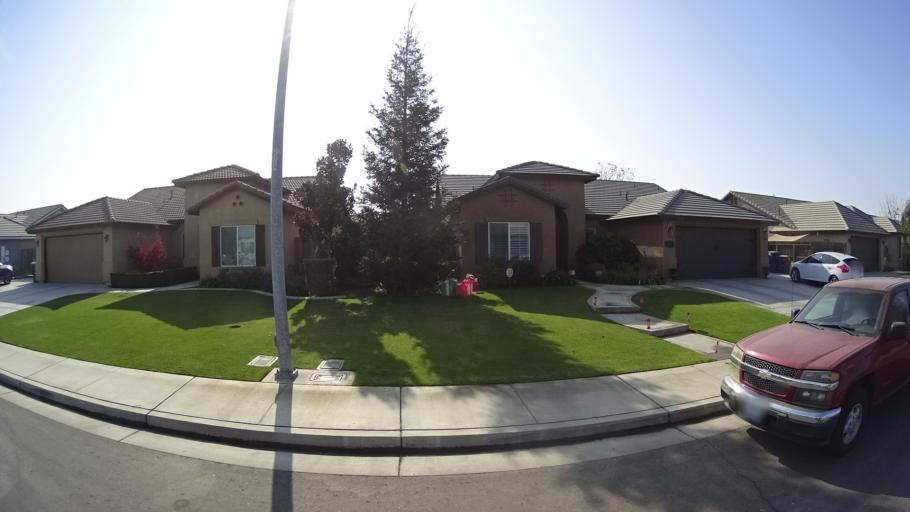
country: US
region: California
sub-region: Kern County
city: Greenacres
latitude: 35.4153
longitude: -119.1229
